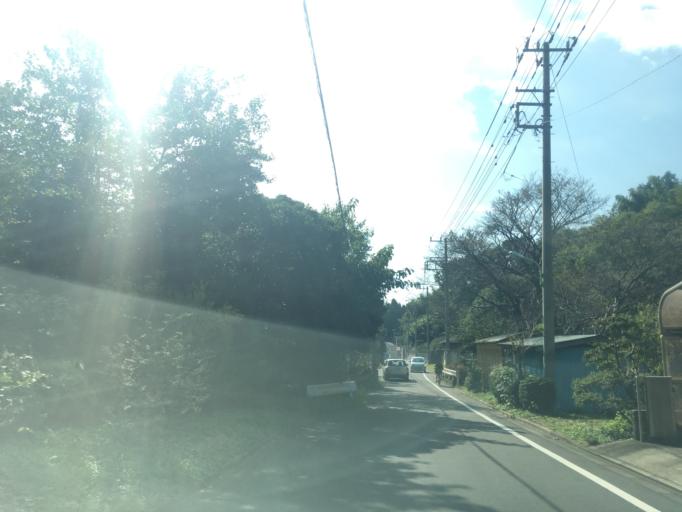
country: JP
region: Tokyo
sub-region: Machida-shi
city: Machida
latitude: 35.5995
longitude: 139.4088
